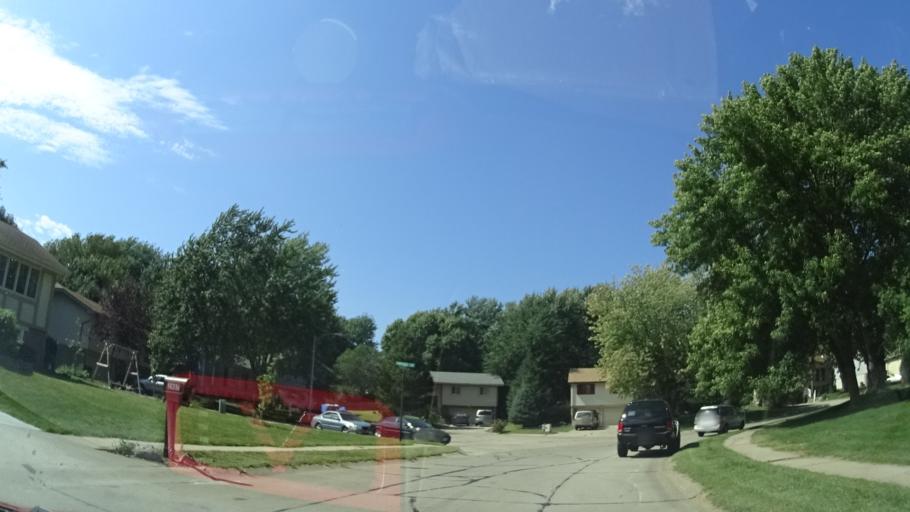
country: US
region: Nebraska
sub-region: Sarpy County
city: Offutt Air Force Base
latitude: 41.1315
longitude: -95.9551
